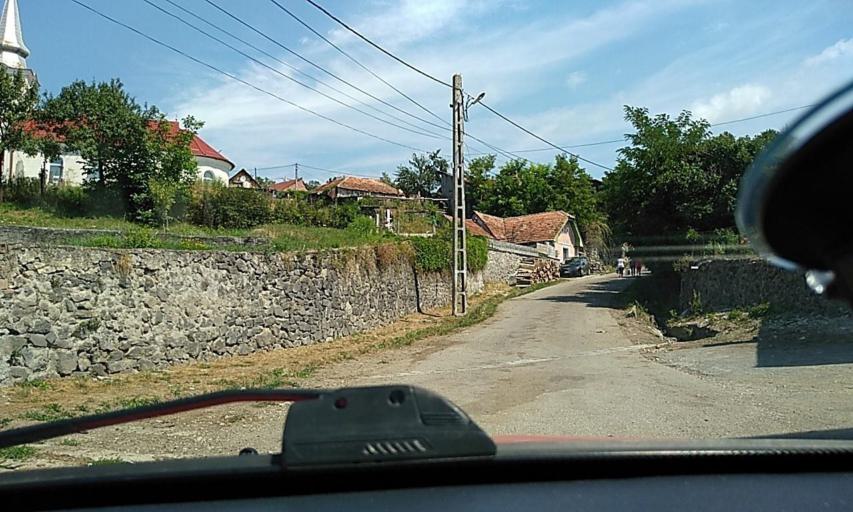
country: RO
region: Brasov
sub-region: Comuna Hoghiz
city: Hoghiz
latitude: 46.0253
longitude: 25.4120
